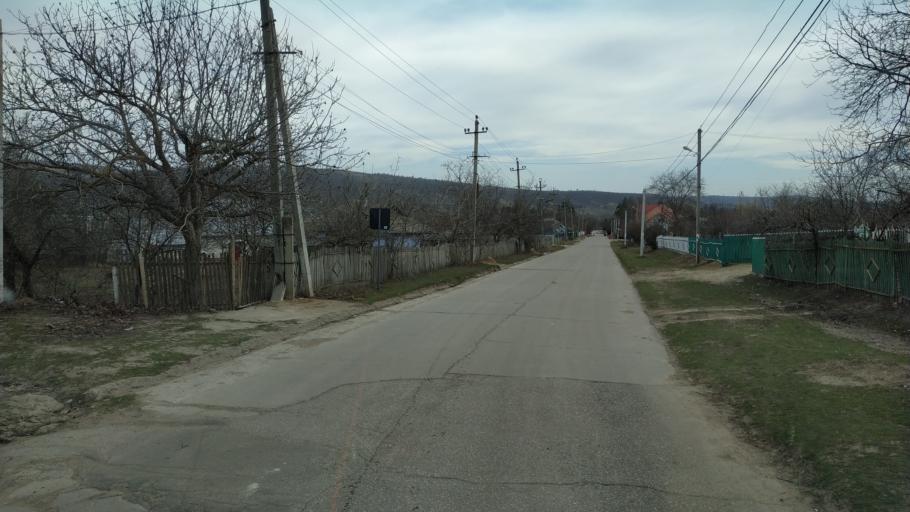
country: MD
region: Hincesti
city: Dancu
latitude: 46.9260
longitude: 28.2634
